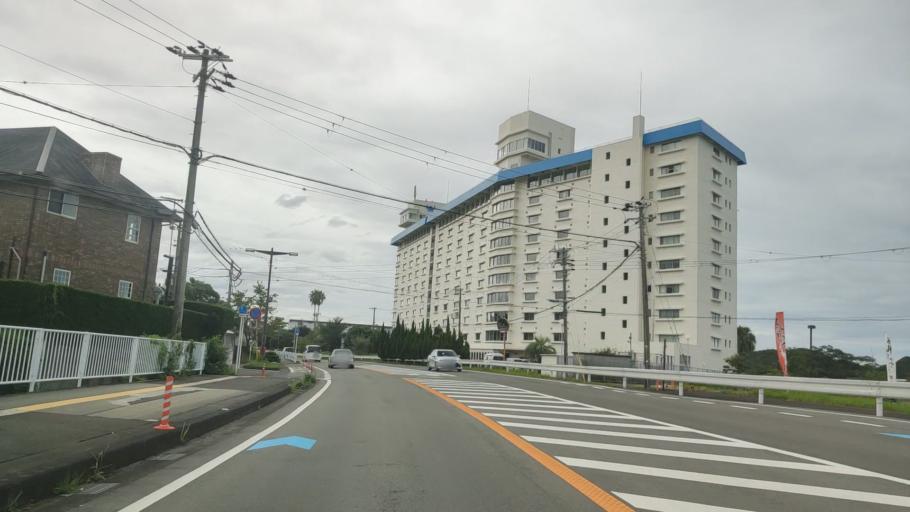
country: JP
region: Wakayama
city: Tanabe
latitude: 33.7003
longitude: 135.3892
